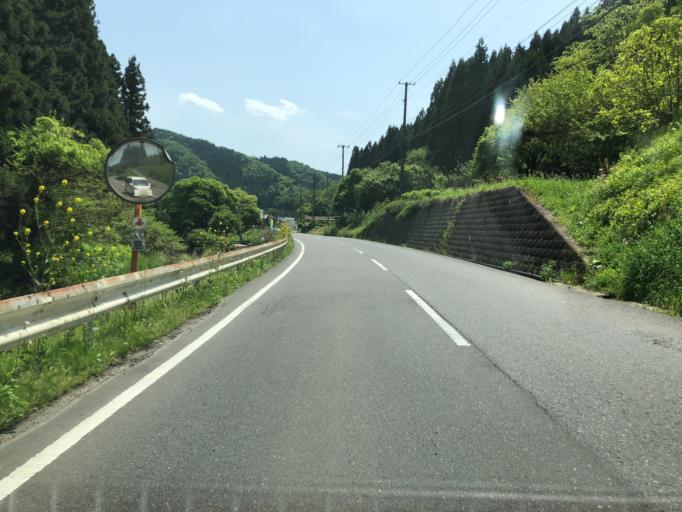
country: JP
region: Fukushima
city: Ishikawa
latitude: 37.1502
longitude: 140.4788
